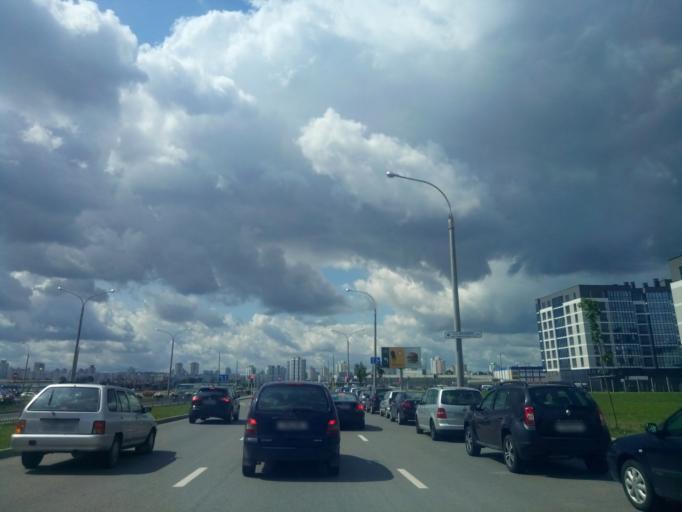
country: BY
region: Minsk
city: Zhdanovichy
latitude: 53.9388
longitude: 27.4537
